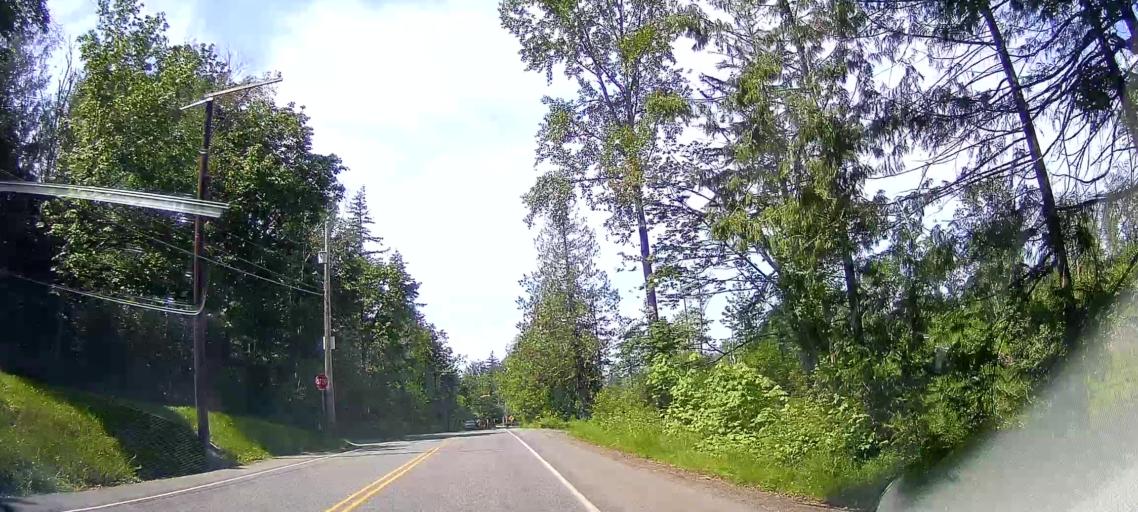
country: US
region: Washington
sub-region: Skagit County
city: Mount Vernon
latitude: 48.4011
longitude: -122.3038
